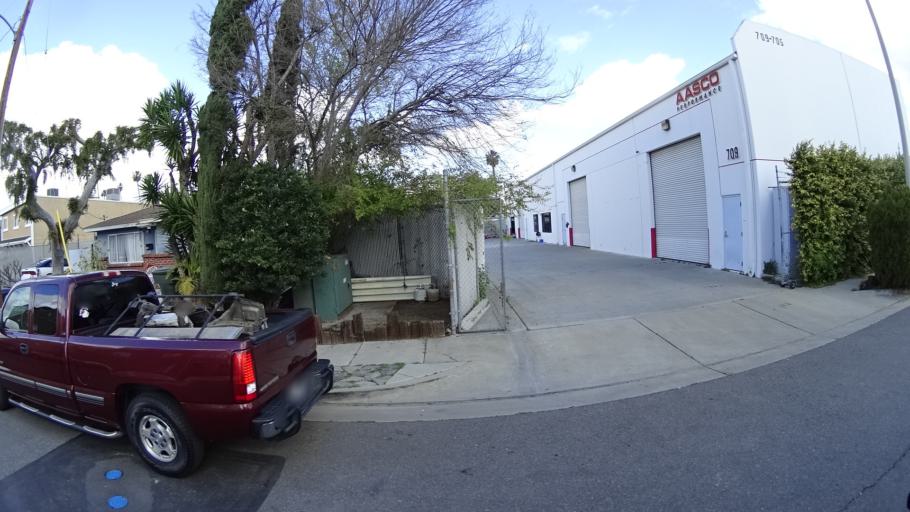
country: US
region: California
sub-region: Orange County
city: Anaheim
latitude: 33.8404
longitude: -117.9078
